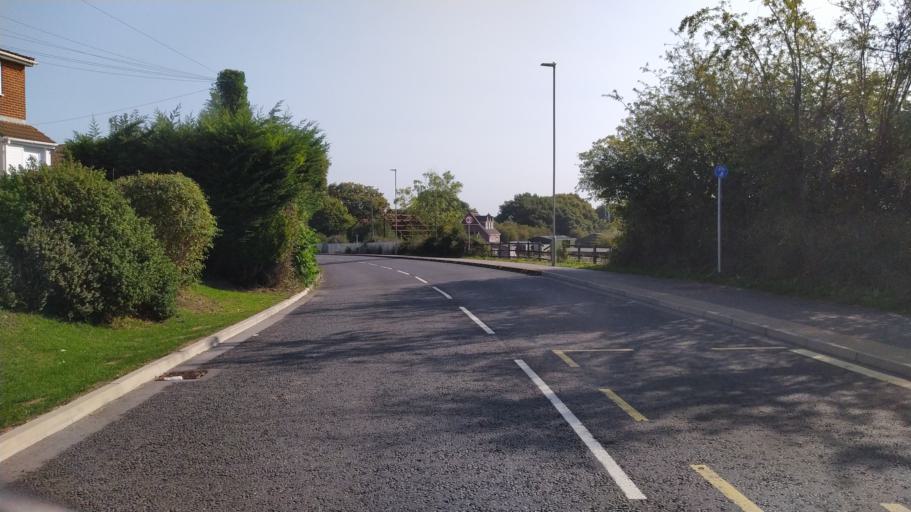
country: GB
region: England
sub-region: Hampshire
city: Hedge End
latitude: 50.9029
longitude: -1.3002
